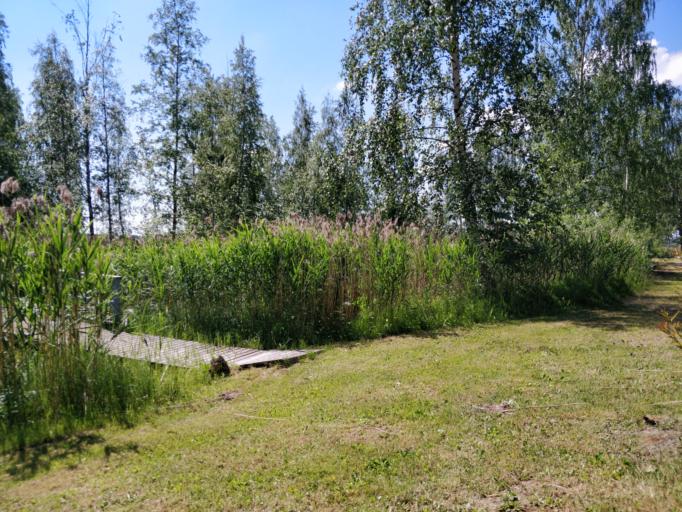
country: FI
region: Haeme
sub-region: Haemeenlinna
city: Tervakoski
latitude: 60.8070
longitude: 24.6133
